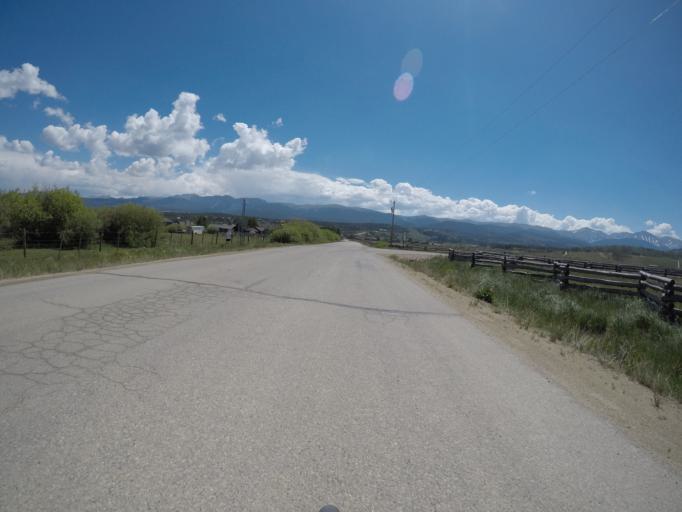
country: US
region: Colorado
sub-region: Grand County
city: Fraser
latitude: 39.9447
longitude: -105.8234
